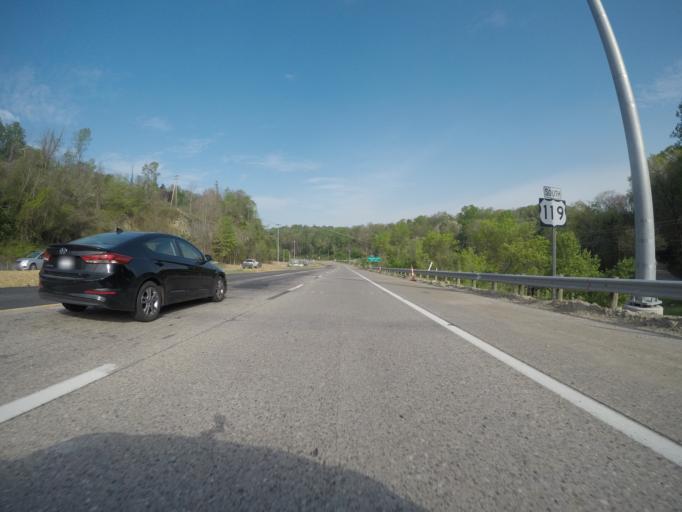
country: US
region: West Virginia
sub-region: Kanawha County
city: Charleston
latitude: 38.3421
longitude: -81.6682
